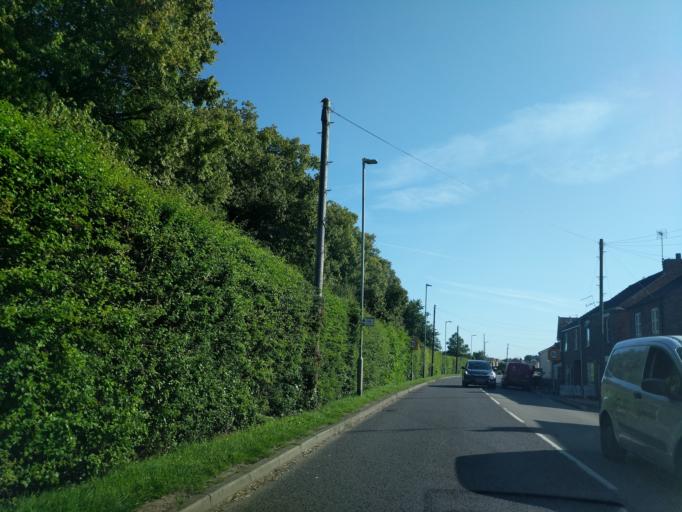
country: GB
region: England
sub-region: Lincolnshire
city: Spalding
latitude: 52.7821
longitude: -0.1763
